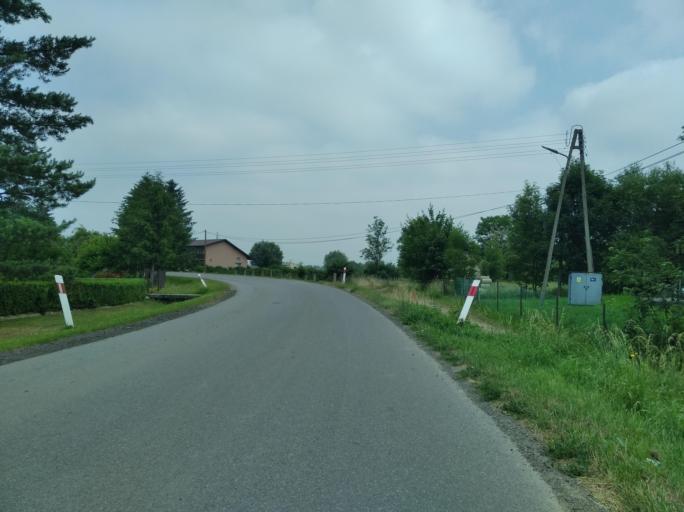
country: PL
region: Subcarpathian Voivodeship
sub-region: Powiat sanocki
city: Besko
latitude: 49.5953
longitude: 21.9617
